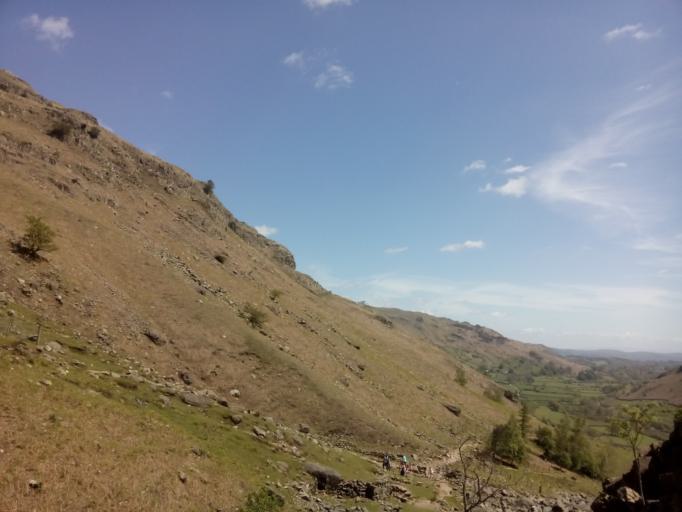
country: GB
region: England
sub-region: Cumbria
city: Ambleside
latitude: 54.4530
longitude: -3.0958
